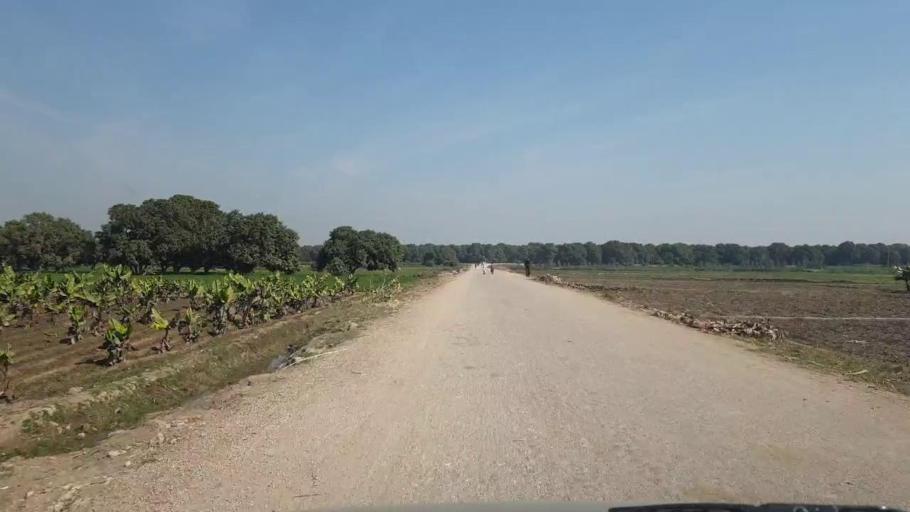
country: PK
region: Sindh
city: Tando Allahyar
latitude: 25.3992
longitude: 68.7723
